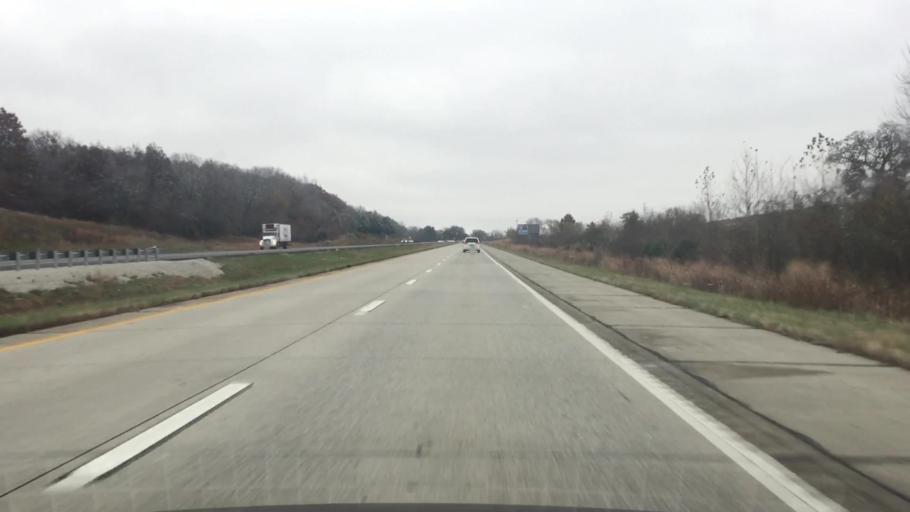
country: US
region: Missouri
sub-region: Saint Clair County
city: Osceola
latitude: 38.0174
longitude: -93.6648
